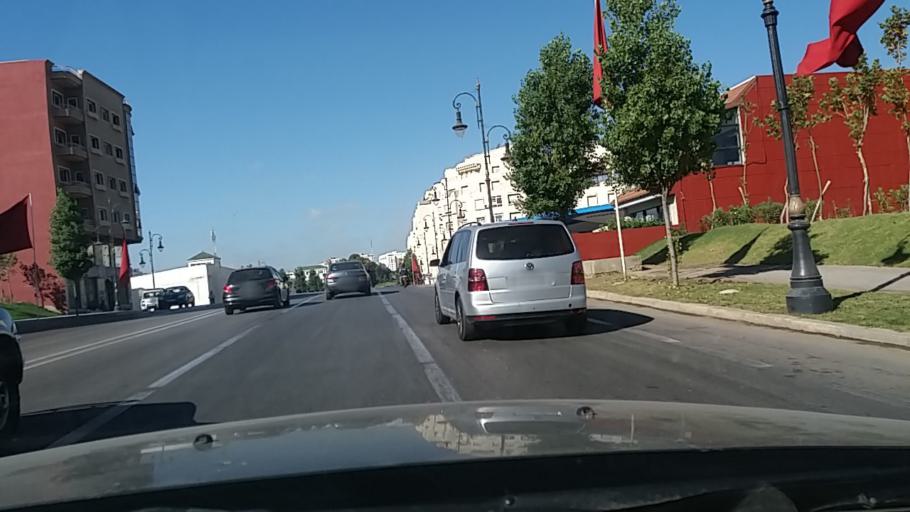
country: MA
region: Tanger-Tetouan
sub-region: Tanger-Assilah
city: Tangier
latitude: 35.7614
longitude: -5.8403
